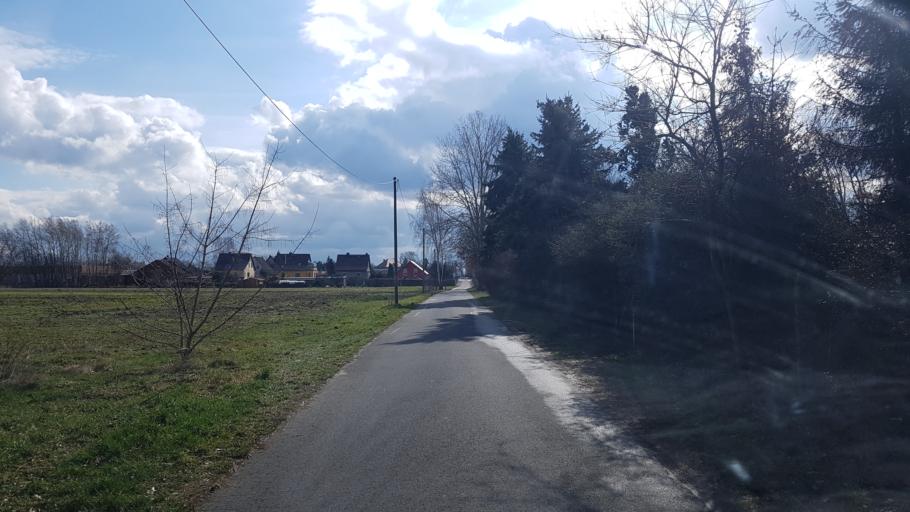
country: DE
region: Brandenburg
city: Elsterwerda
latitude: 51.4681
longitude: 13.5270
